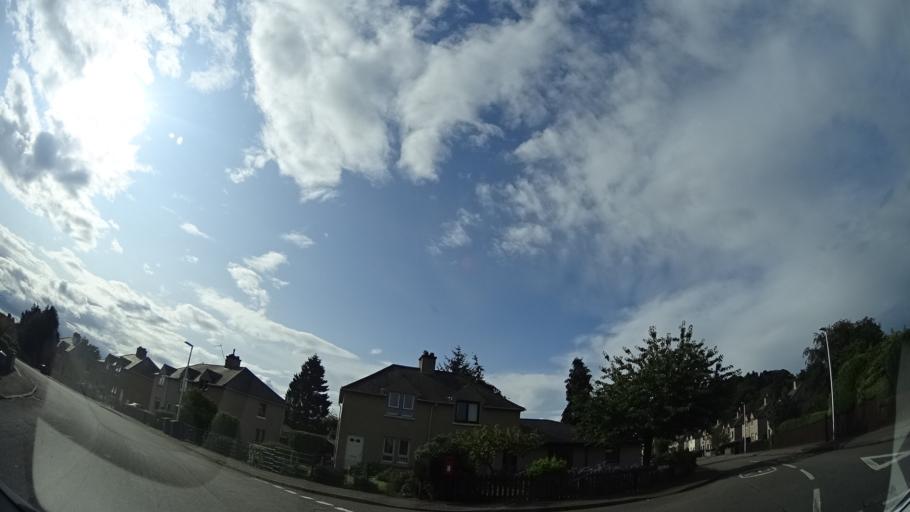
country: GB
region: Scotland
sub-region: Highland
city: Inverness
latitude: 57.4723
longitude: -4.2391
